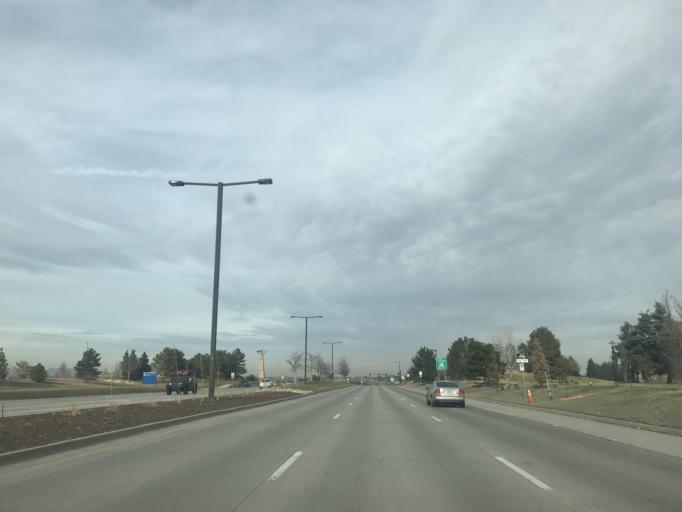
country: US
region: Colorado
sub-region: Douglas County
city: Highlands Ranch
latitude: 39.5560
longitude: -105.0081
